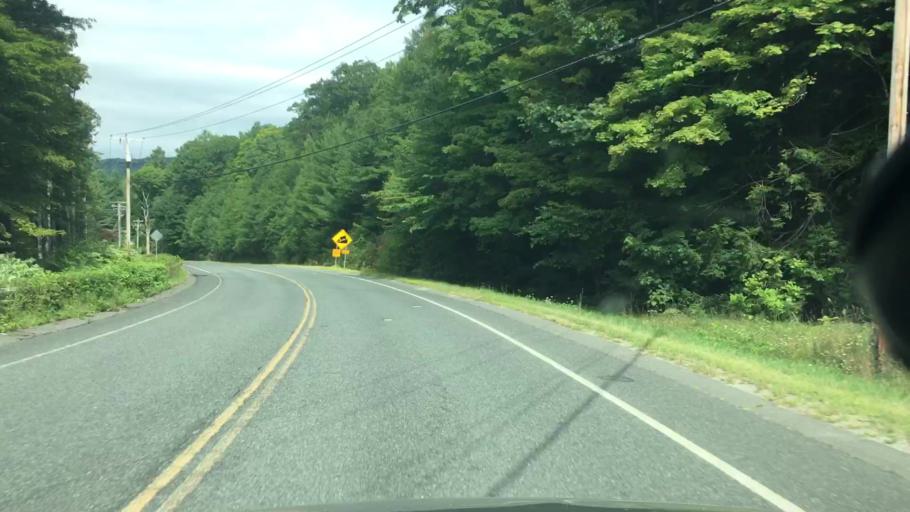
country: US
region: Massachusetts
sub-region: Franklin County
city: Colrain
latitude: 42.6676
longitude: -72.6834
